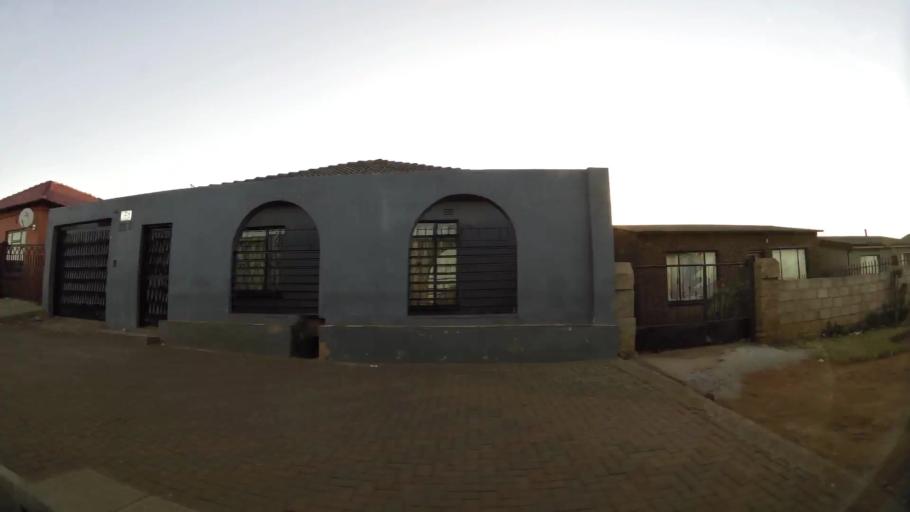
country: ZA
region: Gauteng
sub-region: Ekurhuleni Metropolitan Municipality
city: Tembisa
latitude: -25.9968
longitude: 28.2268
